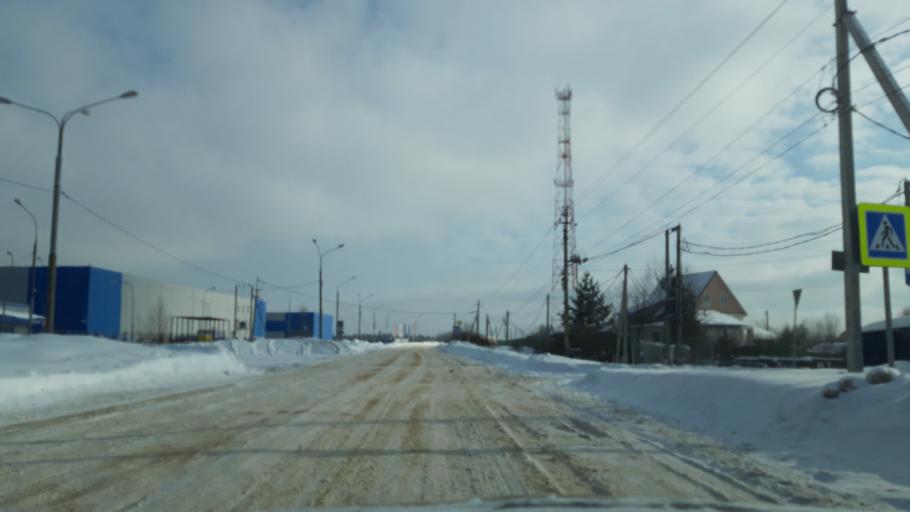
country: RU
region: Moskovskaya
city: Yermolino
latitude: 56.1437
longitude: 37.3766
